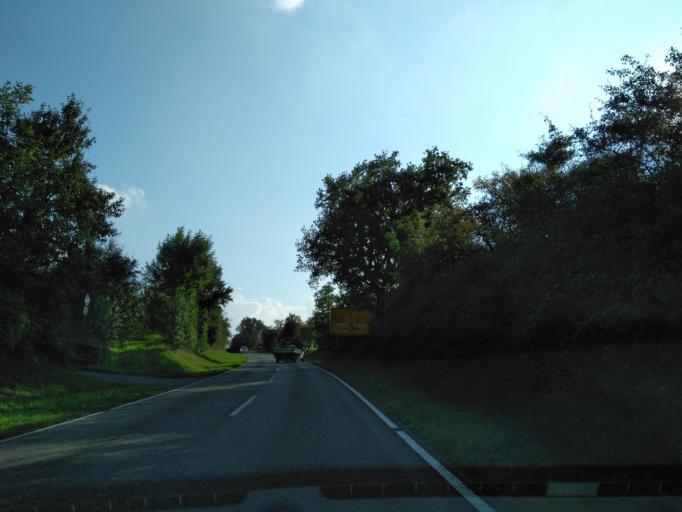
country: DE
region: Baden-Wuerttemberg
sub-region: Regierungsbezirk Stuttgart
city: Sersheim
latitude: 48.9526
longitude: 9.0179
